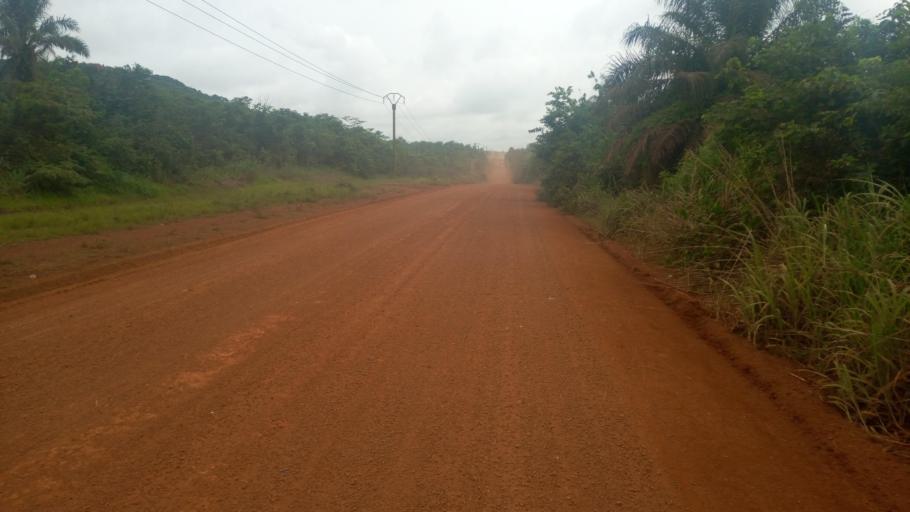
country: SL
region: Southern Province
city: Mogbwemo
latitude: 7.7087
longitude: -12.2847
